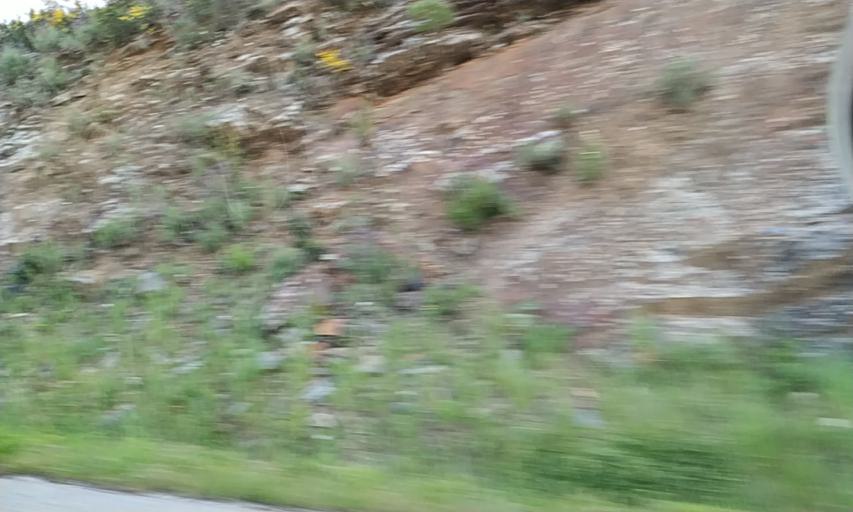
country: PT
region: Portalegre
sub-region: Portalegre
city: Sao Juliao
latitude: 39.3578
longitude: -7.3168
